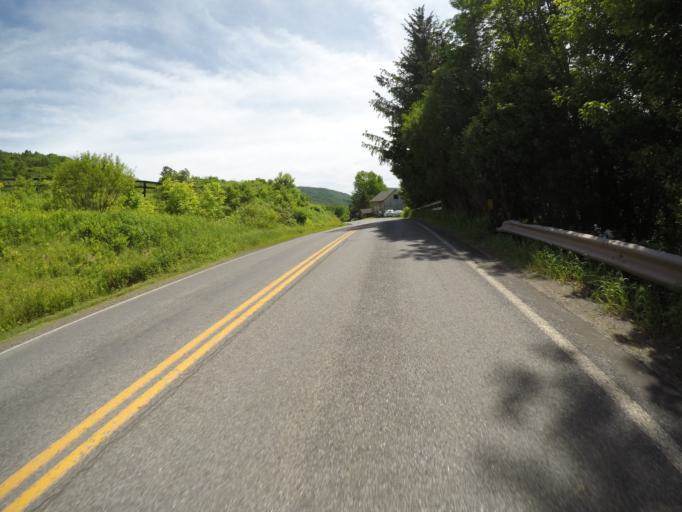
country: US
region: New York
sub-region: Delaware County
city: Delhi
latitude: 42.1572
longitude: -74.7980
